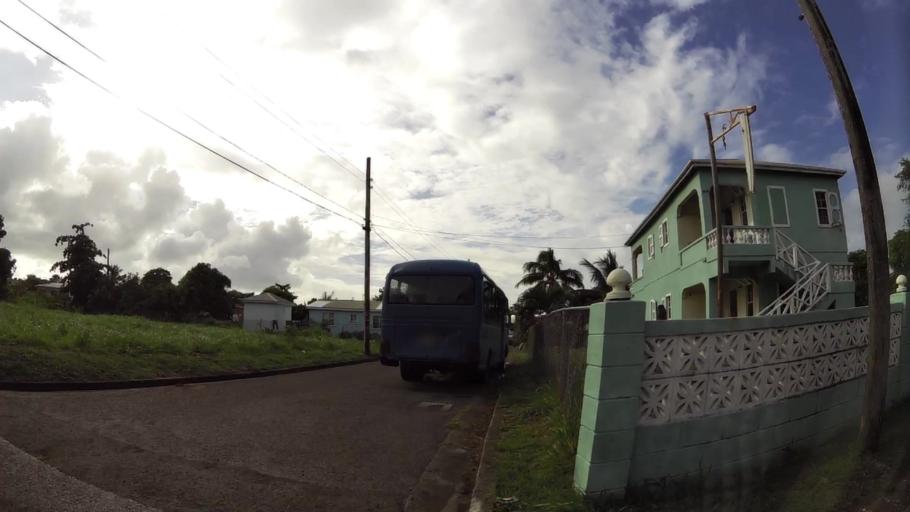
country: AG
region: Saint John
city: Saint John's
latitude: 17.1269
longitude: -61.8278
